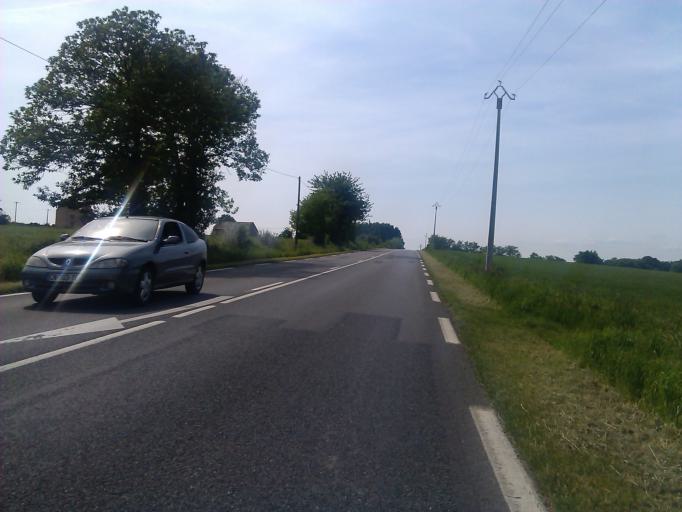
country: FR
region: Centre
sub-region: Departement du Cher
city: Chateaumeillant
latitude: 46.5537
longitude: 2.0881
